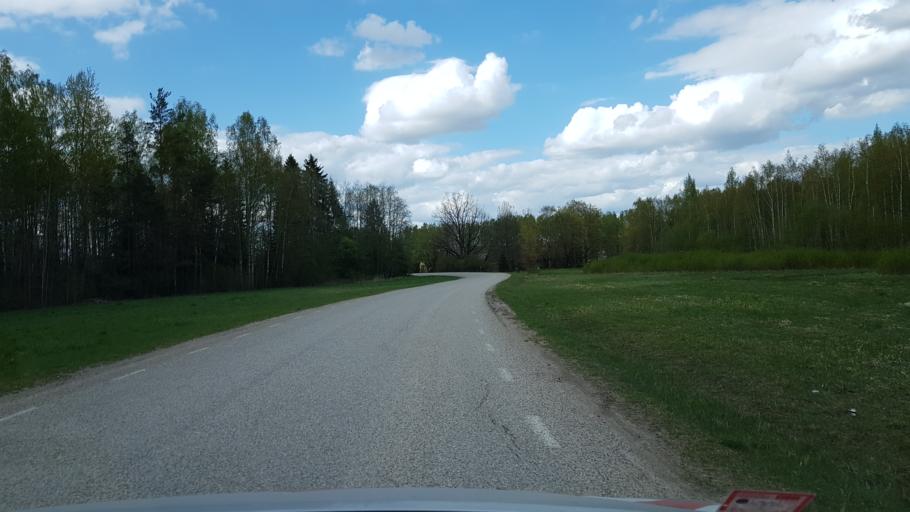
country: EE
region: Tartu
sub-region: Tartu linn
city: Tartu
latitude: 58.3507
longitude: 26.8046
